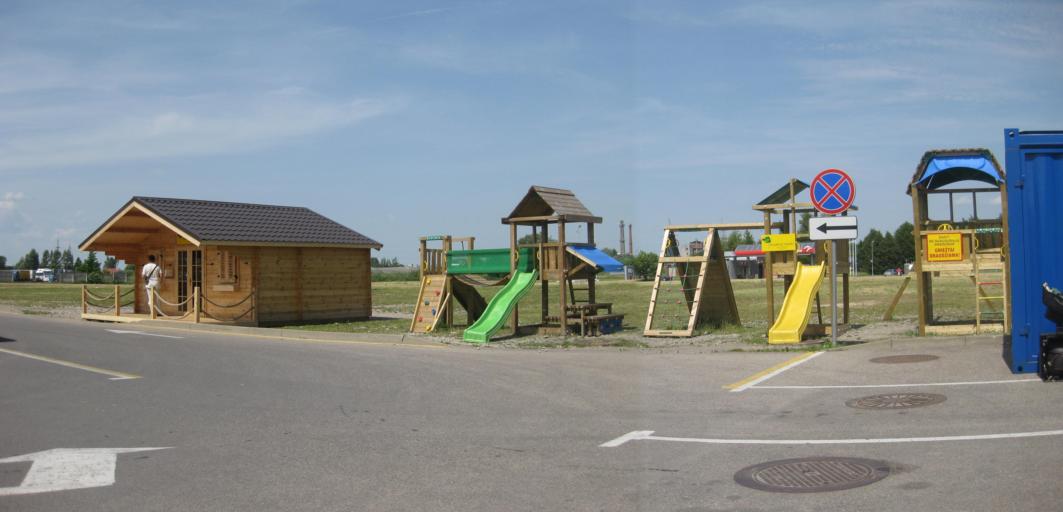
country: LT
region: Kauno apskritis
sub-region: Kaunas
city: Aleksotas
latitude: 54.8659
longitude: 23.8874
